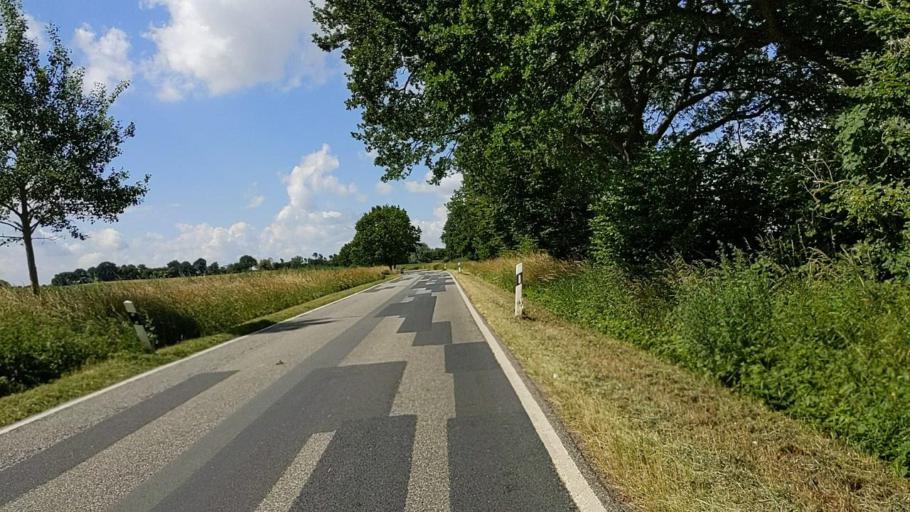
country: DE
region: Mecklenburg-Vorpommern
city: Selmsdorf
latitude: 53.8572
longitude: 10.8133
